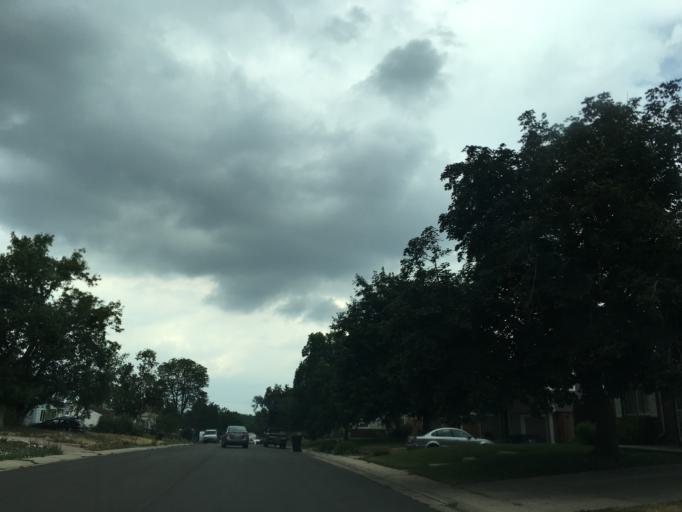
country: US
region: Colorado
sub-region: Arapahoe County
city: Sheridan
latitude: 39.6846
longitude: -105.0139
